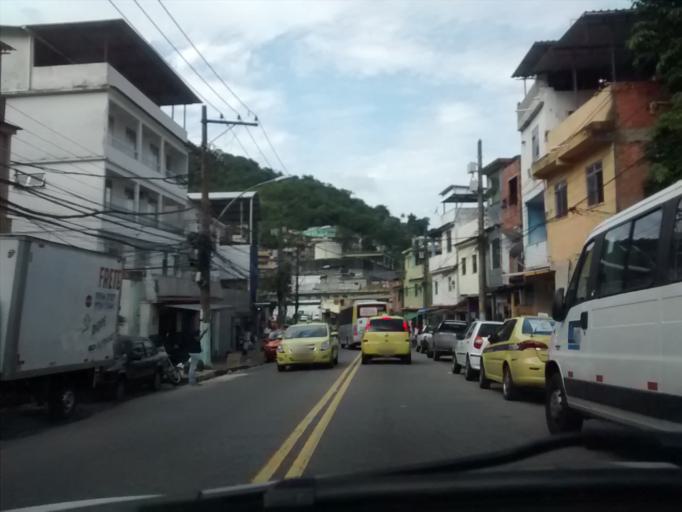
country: BR
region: Rio de Janeiro
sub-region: Rio De Janeiro
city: Rio de Janeiro
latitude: -22.9419
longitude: -43.2540
